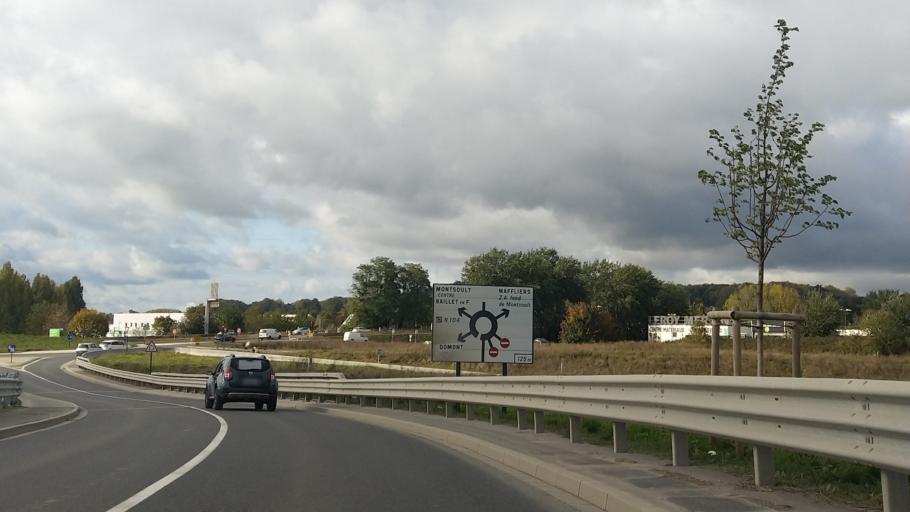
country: FR
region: Ile-de-France
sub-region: Departement du Val-d'Oise
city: Montsoult
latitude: 49.0668
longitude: 2.3317
